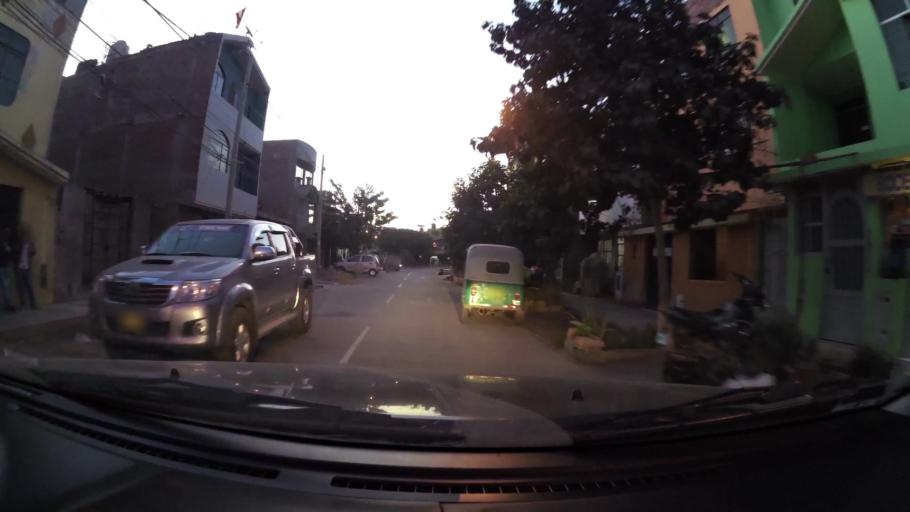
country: PE
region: Ica
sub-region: Provincia de Ica
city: Ica
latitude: -14.0810
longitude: -75.7348
